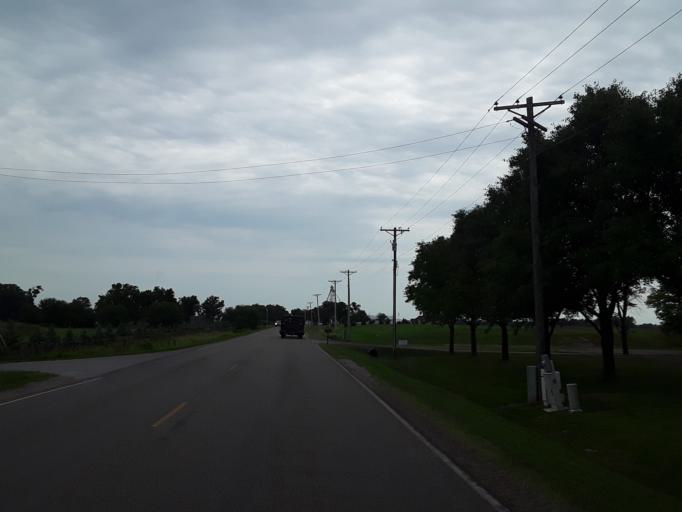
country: US
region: Nebraska
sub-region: Douglas County
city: Valley
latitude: 41.2582
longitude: -96.3305
